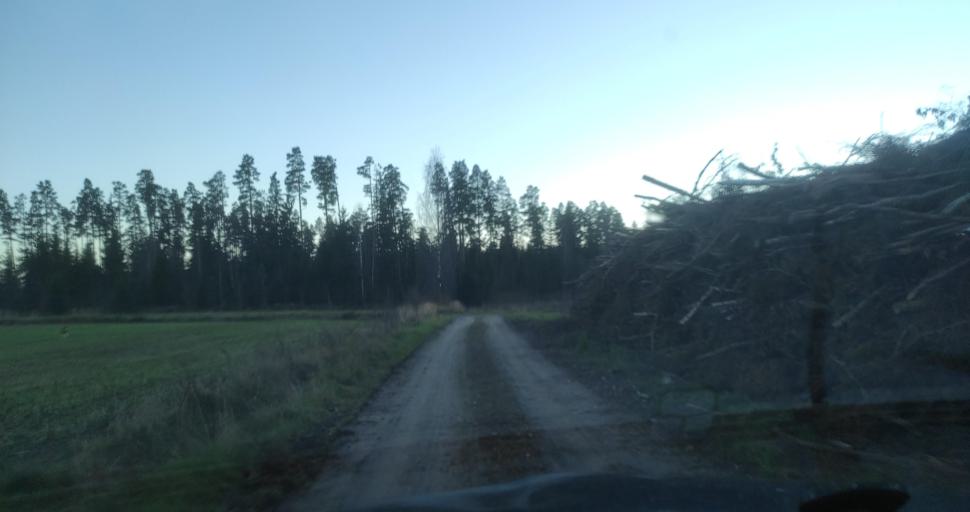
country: LV
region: Dundaga
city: Dundaga
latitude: 57.3710
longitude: 22.2240
